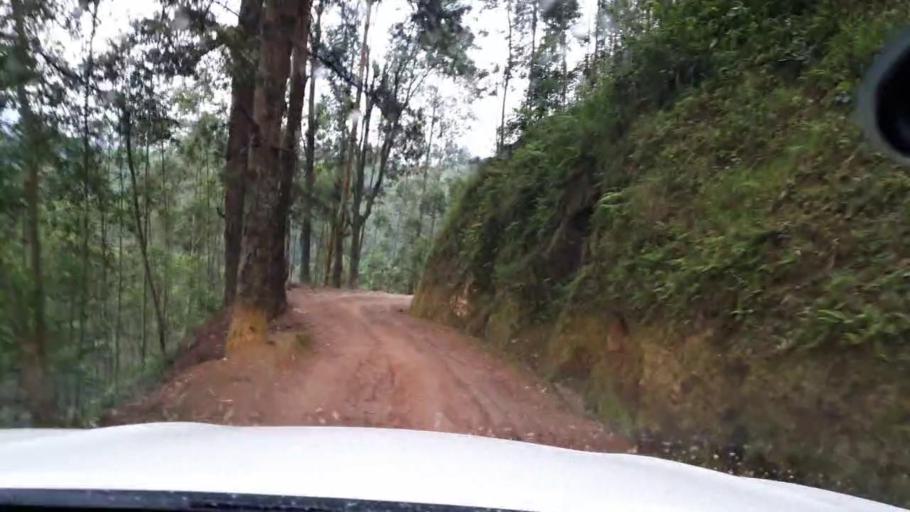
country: RW
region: Western Province
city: Cyangugu
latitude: -2.4125
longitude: 29.1951
